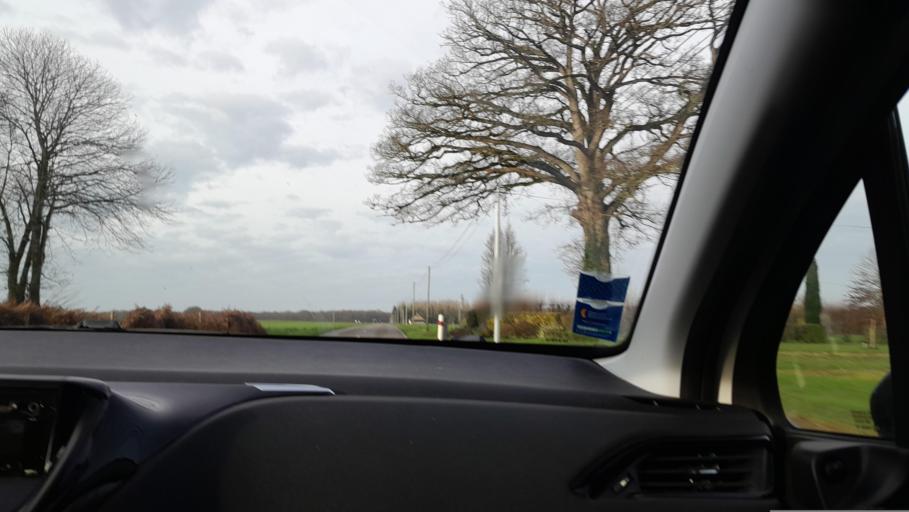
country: FR
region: Brittany
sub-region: Departement d'Ille-et-Vilaine
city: La Guerche-de-Bretagne
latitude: 47.9016
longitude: -1.1659
